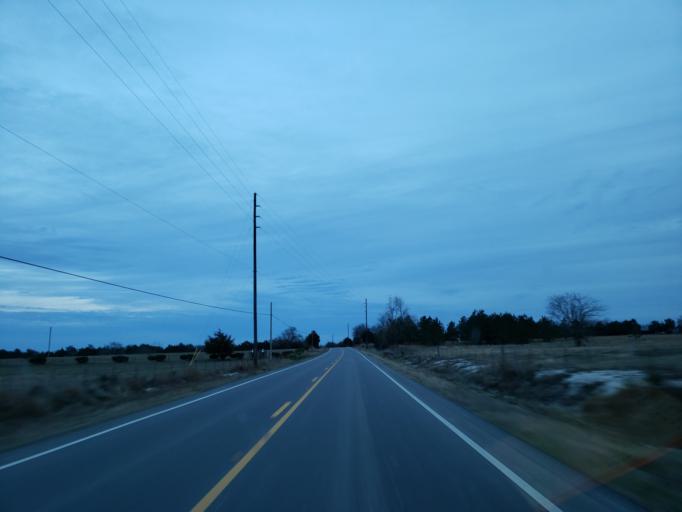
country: US
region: Alabama
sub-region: Sumter County
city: Livingston
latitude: 32.8117
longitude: -88.2728
